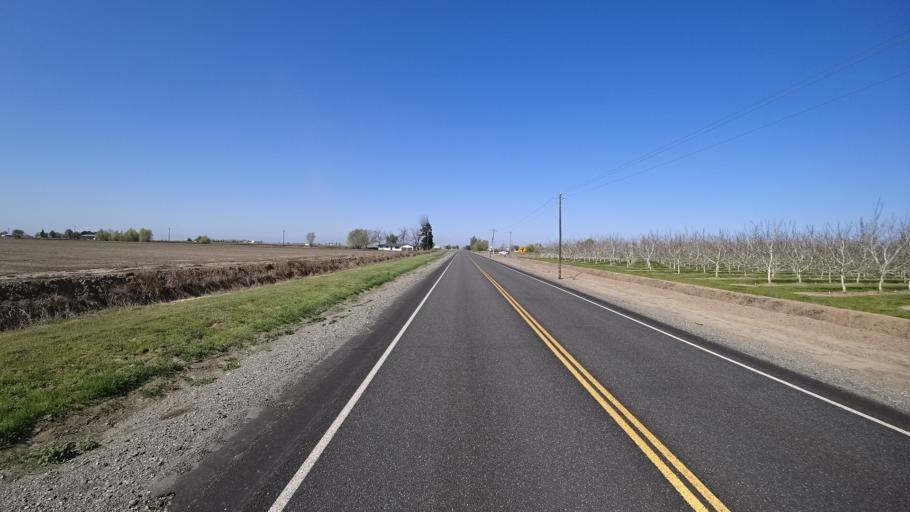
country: US
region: California
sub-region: Glenn County
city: Willows
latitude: 39.4574
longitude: -122.0290
